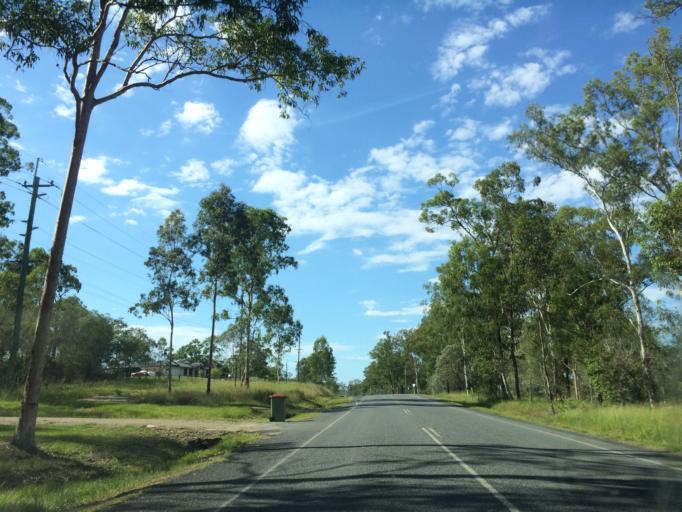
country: AU
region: Queensland
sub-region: Logan
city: North Maclean
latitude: -27.7515
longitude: 152.9867
